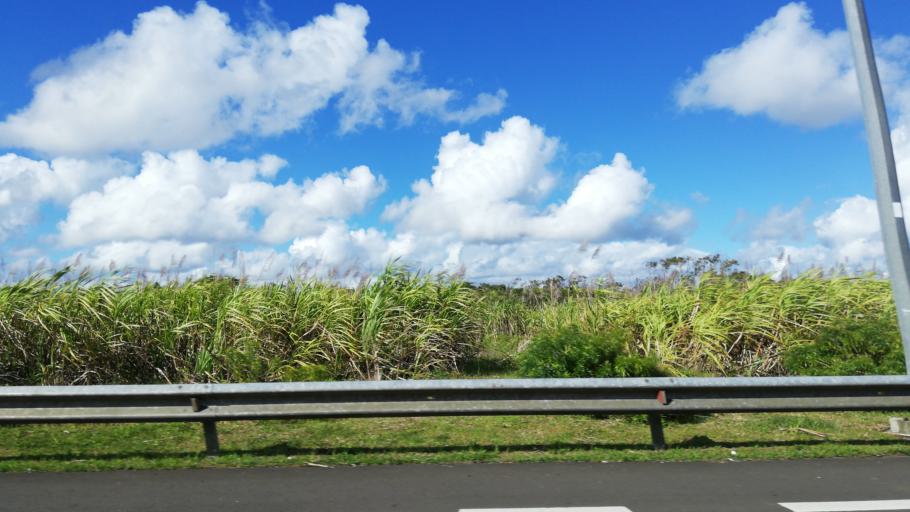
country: MU
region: Moka
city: Quartier Militaire
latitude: -20.2553
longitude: 57.5788
